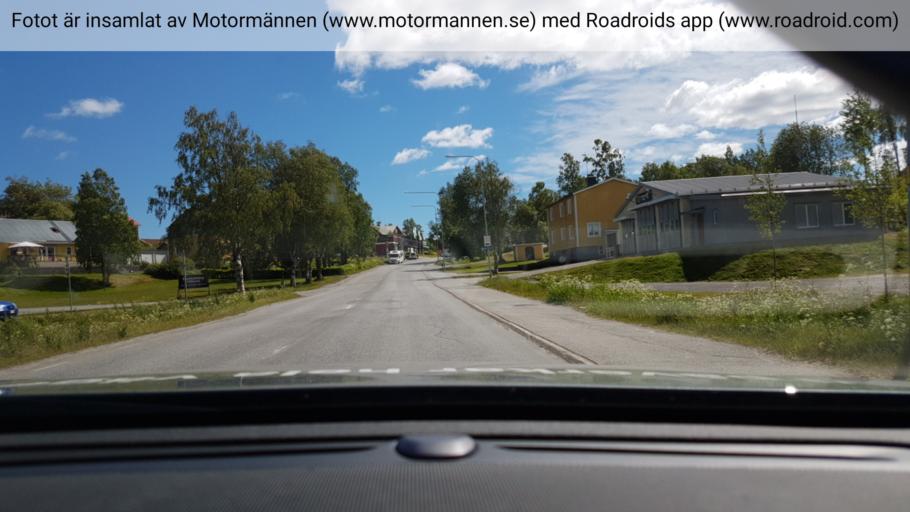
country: SE
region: Vaesterbotten
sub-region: Skelleftea Kommun
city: Burea
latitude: 64.3713
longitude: 21.3076
